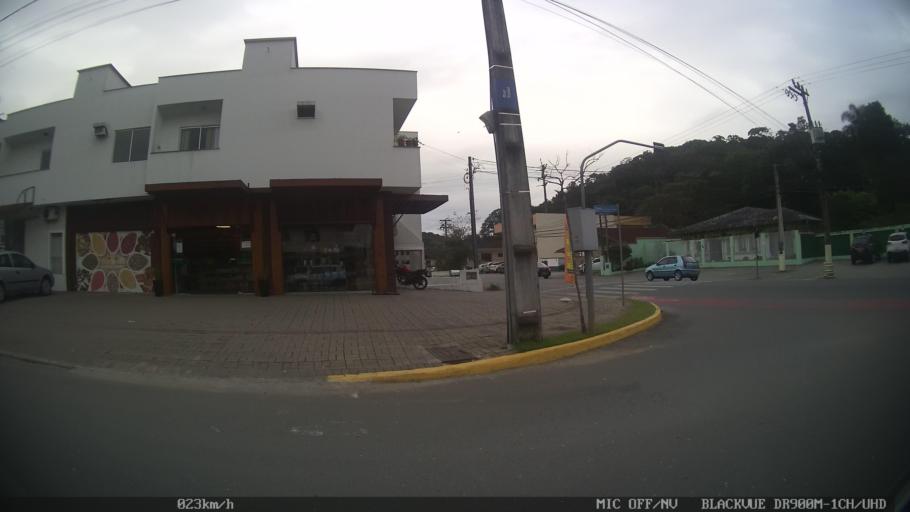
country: BR
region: Santa Catarina
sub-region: Joinville
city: Joinville
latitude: -26.2926
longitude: -48.8678
